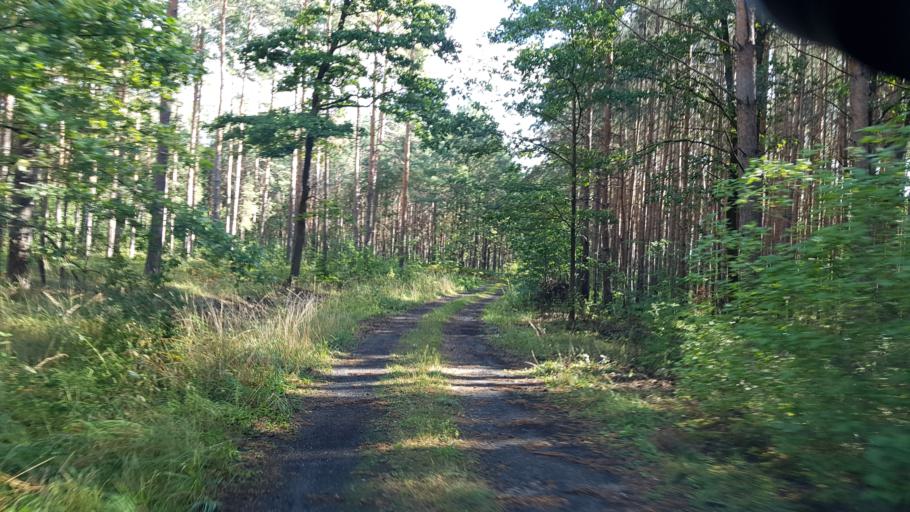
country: DE
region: Brandenburg
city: Tschernitz
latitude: 51.6287
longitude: 14.5815
